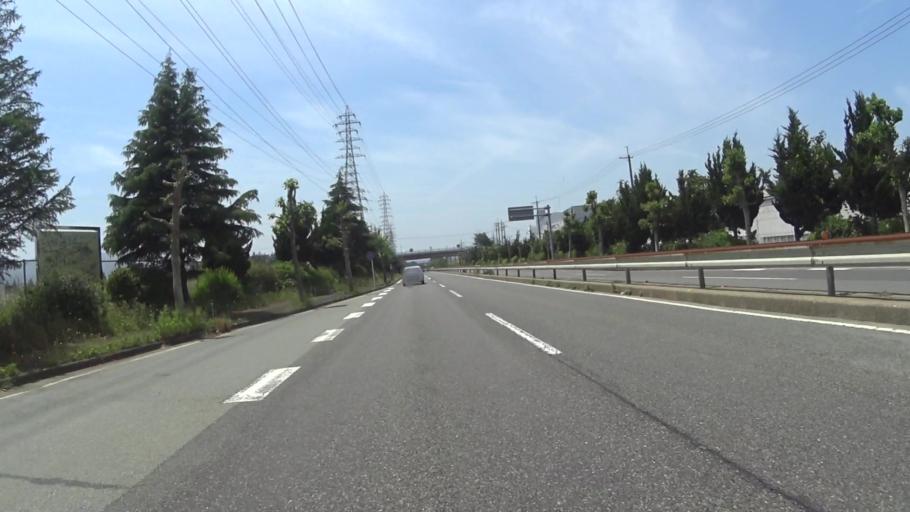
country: JP
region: Kyoto
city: Fukuchiyama
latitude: 35.2851
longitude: 135.1682
